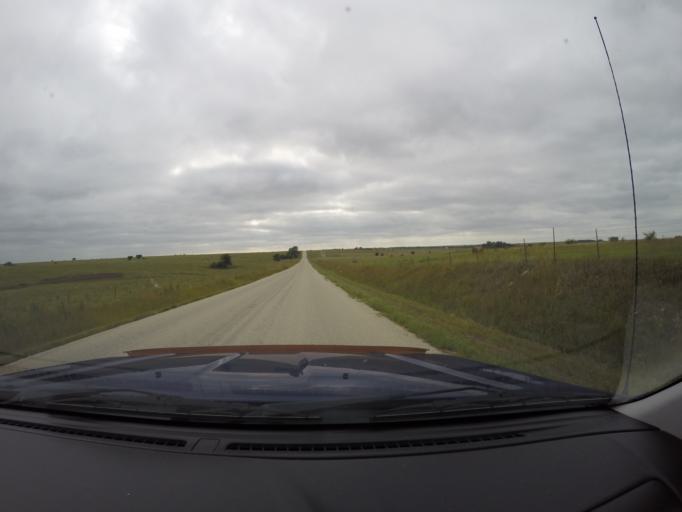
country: US
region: Kansas
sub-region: Dickinson County
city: Herington
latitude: 38.7975
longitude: -96.7607
